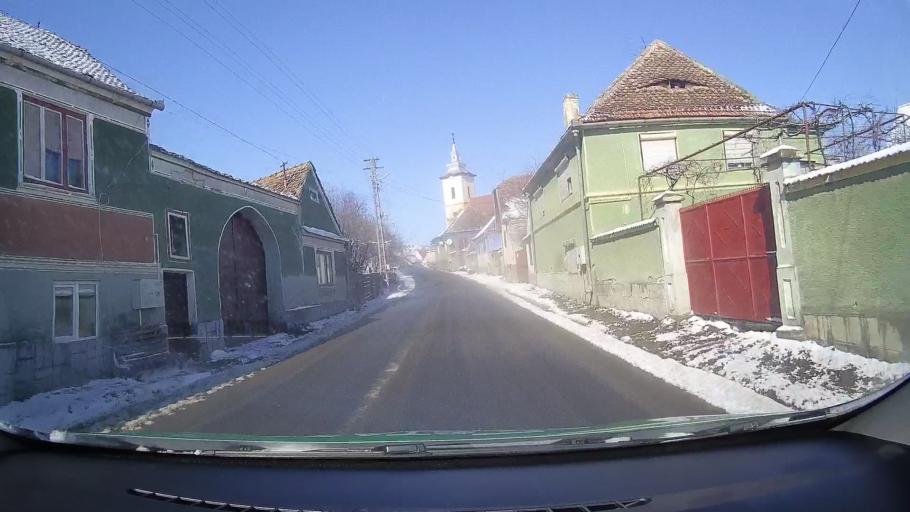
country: RO
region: Sibiu
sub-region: Comuna Avrig
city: Avrig
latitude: 45.7614
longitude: 24.3889
